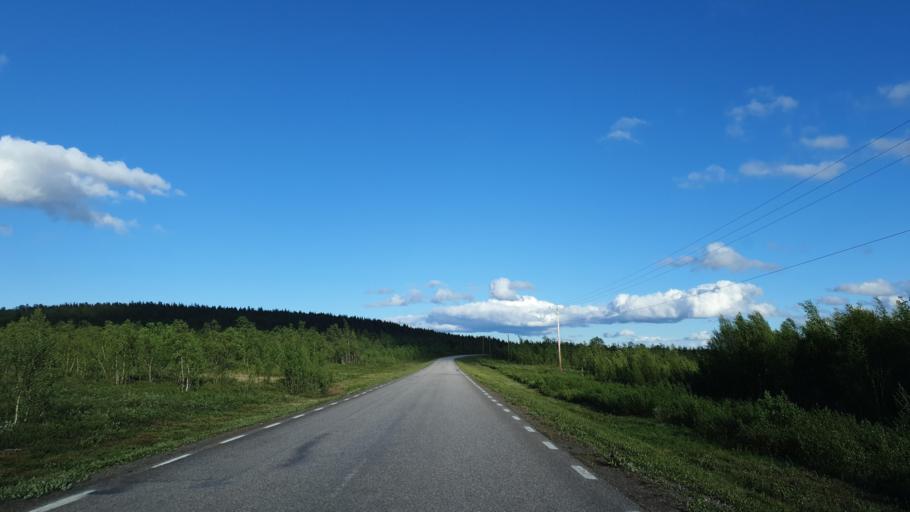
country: SE
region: Norrbotten
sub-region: Kiruna Kommun
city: Kiruna
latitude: 67.7596
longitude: 20.0127
